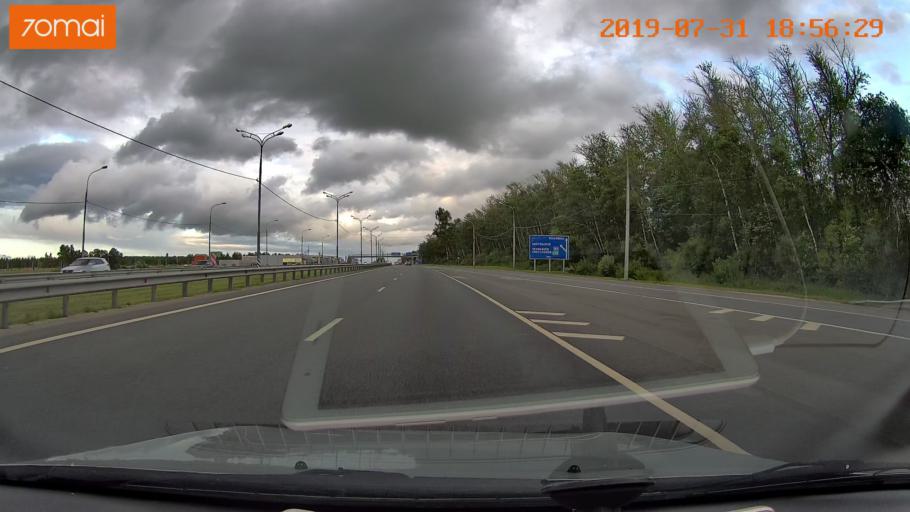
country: RU
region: Moskovskaya
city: Raduzhnyy
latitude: 55.1627
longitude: 38.6786
